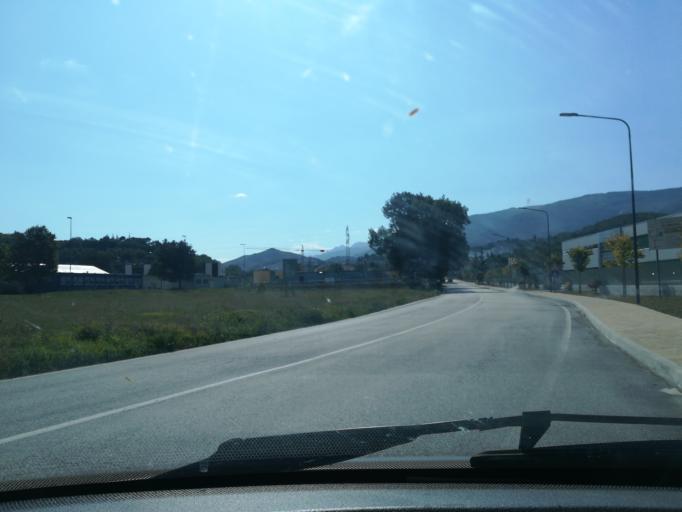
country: IT
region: The Marches
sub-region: Provincia di Macerata
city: Caldarola
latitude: 43.1479
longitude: 13.2241
